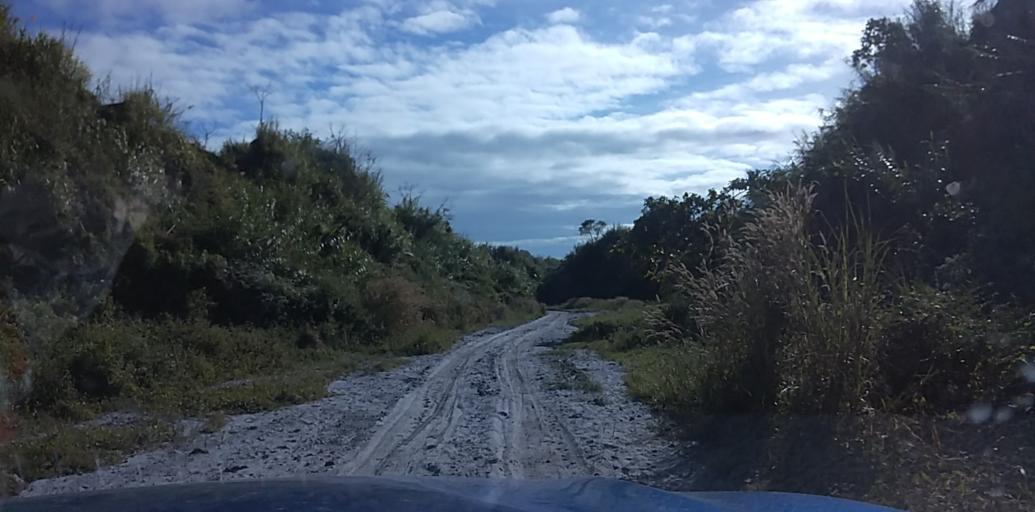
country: PH
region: Central Luzon
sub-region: Province of Pampanga
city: Babo-Pangulo
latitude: 15.1501
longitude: 120.4347
